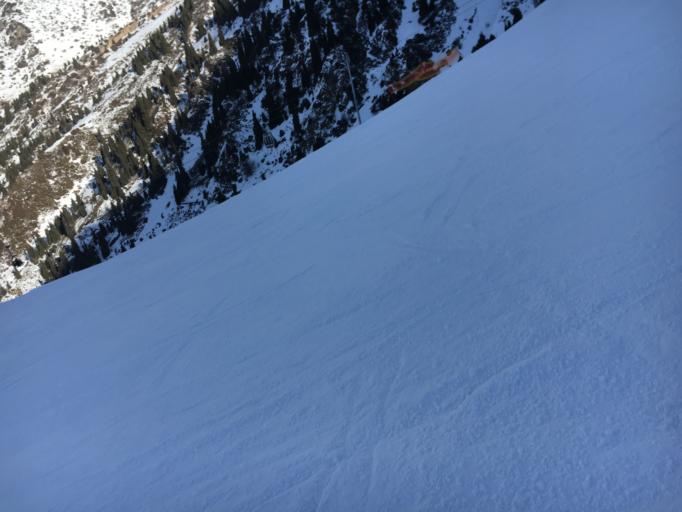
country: KZ
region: Almaty Qalasy
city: Almaty
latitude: 43.1199
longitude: 77.0964
